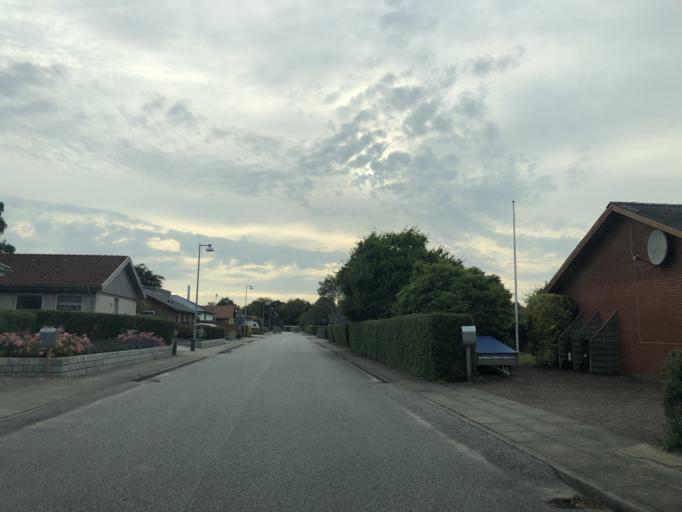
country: DK
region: Central Jutland
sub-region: Herning Kommune
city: Herning
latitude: 56.1477
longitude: 8.9527
